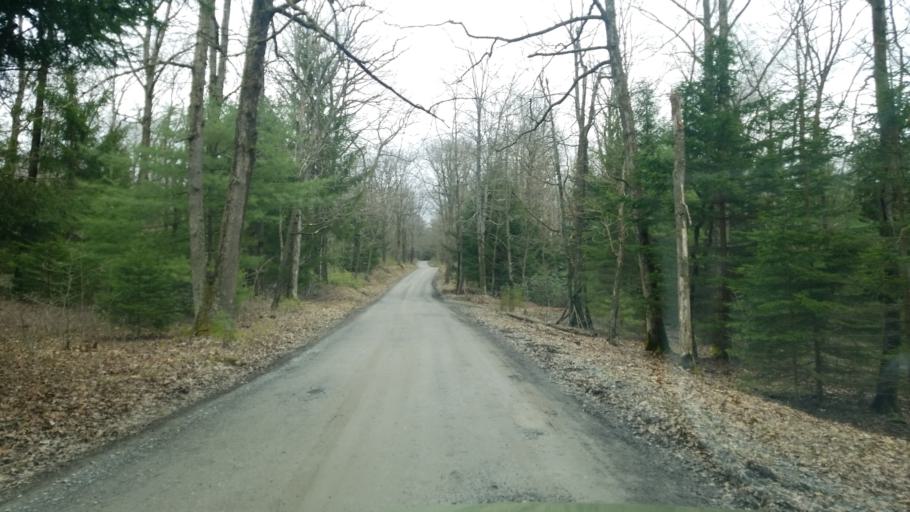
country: US
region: Pennsylvania
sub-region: Clearfield County
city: Shiloh
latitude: 41.1703
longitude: -78.2834
